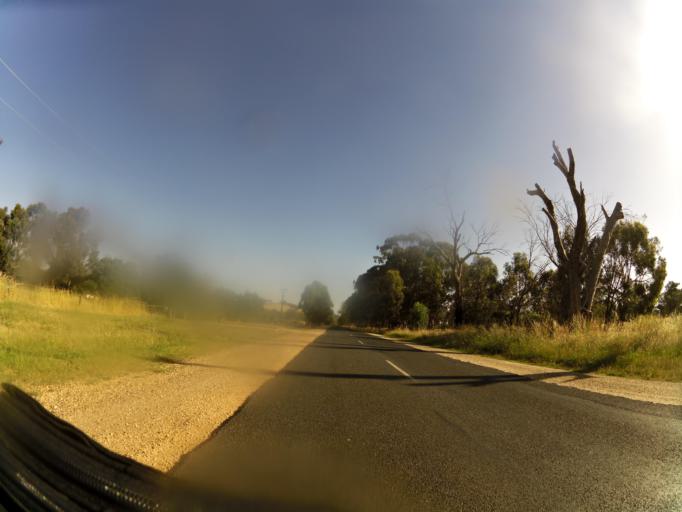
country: AU
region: Victoria
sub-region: Murrindindi
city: Kinglake West
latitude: -36.9931
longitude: 145.1127
